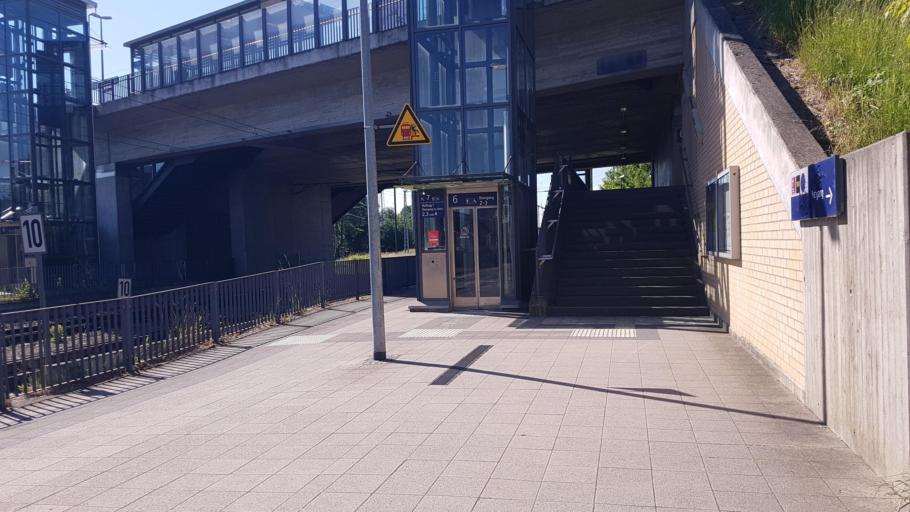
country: DE
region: Brandenburg
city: Falkenberg
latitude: 51.5835
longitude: 13.2469
